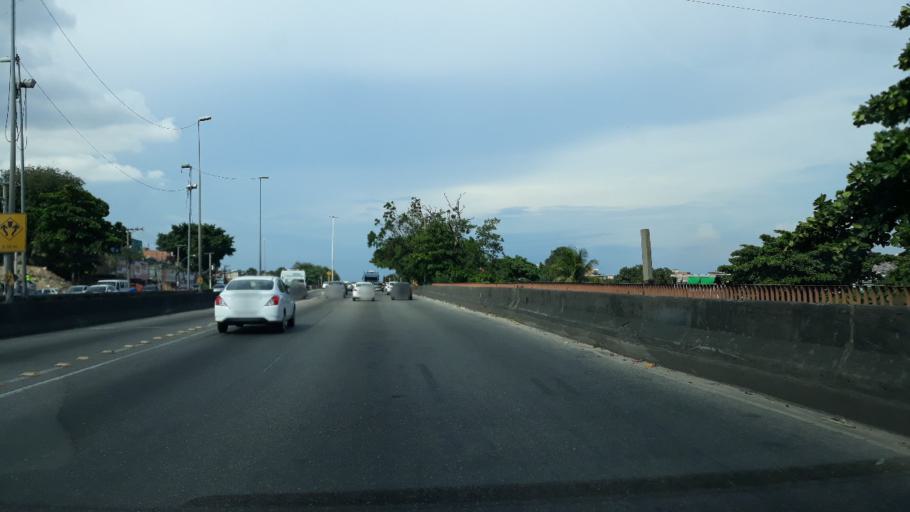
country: BR
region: Rio de Janeiro
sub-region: Sao Joao De Meriti
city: Sao Joao de Meriti
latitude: -22.8384
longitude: -43.3662
